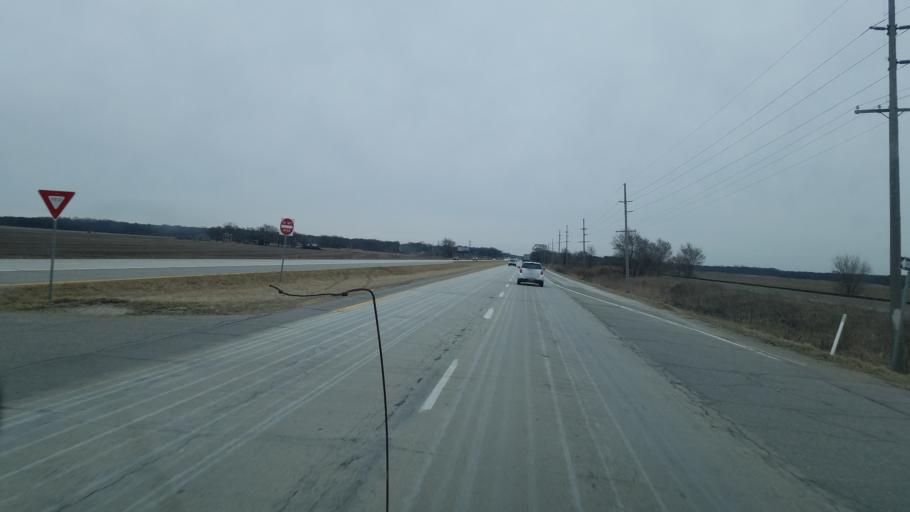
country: US
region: Indiana
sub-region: Starke County
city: Koontz Lake
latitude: 41.3755
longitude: -86.5339
